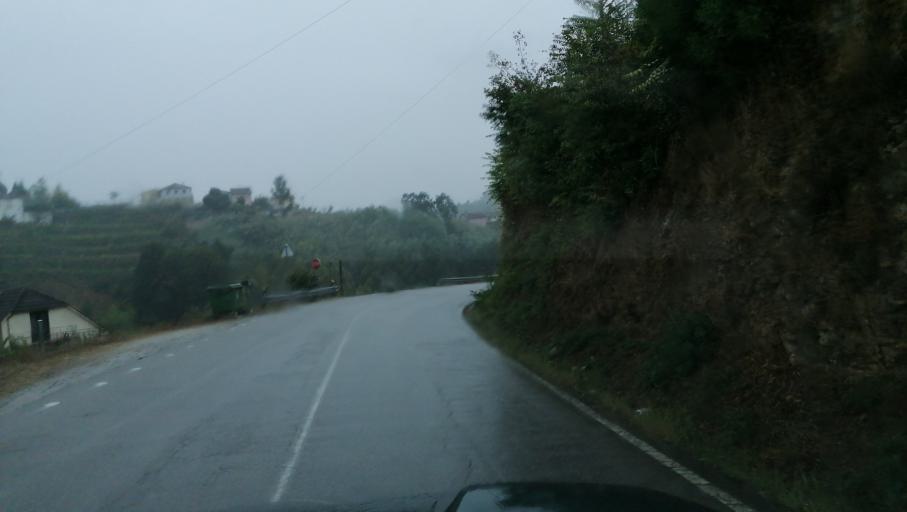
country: PT
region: Braga
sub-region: Cabeceiras de Basto
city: Cabeceiras de Basto
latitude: 41.4878
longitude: -7.9572
